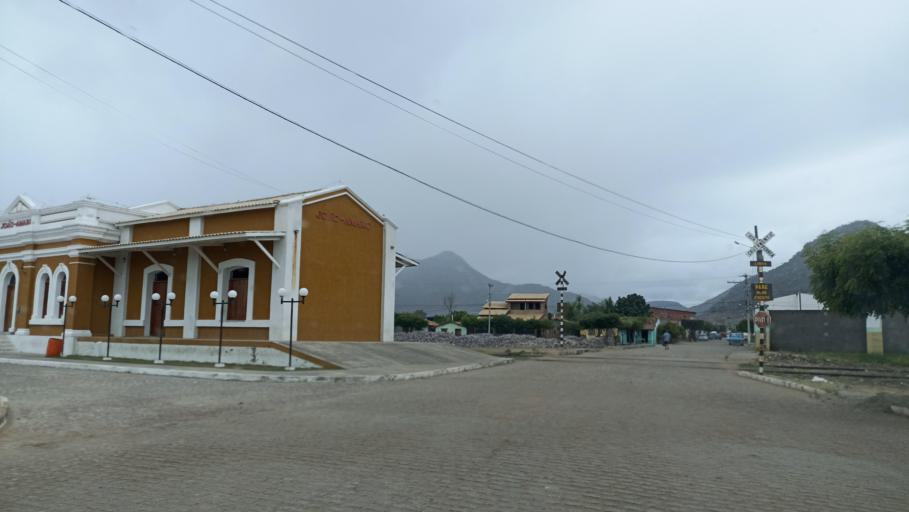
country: BR
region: Bahia
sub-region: Iacu
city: Iacu
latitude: -12.7978
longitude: -40.3514
